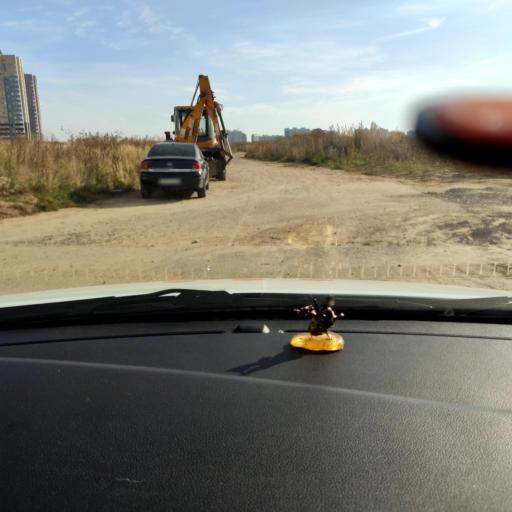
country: RU
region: Tatarstan
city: Osinovo
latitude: 55.8630
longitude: 48.8731
